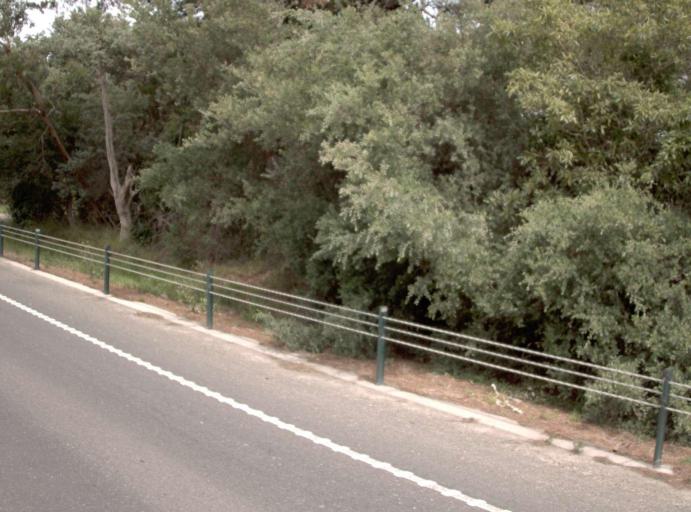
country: AU
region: Victoria
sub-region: Mornington Peninsula
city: Tyabb
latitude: -38.2554
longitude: 145.2120
